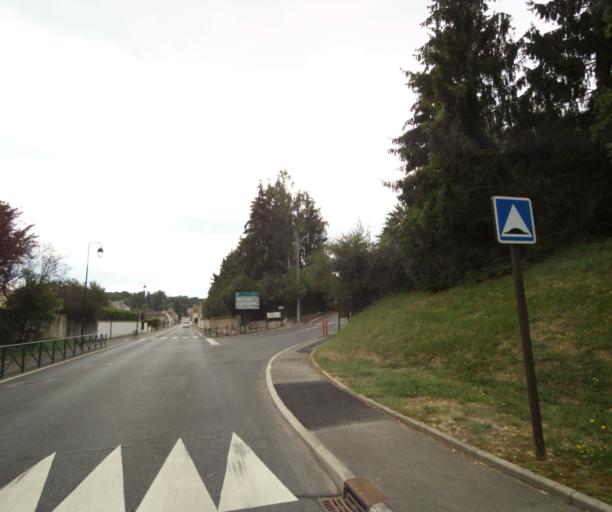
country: FR
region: Ile-de-France
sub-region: Departement de Seine-et-Marne
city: Cely
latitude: 48.4586
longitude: 2.5242
